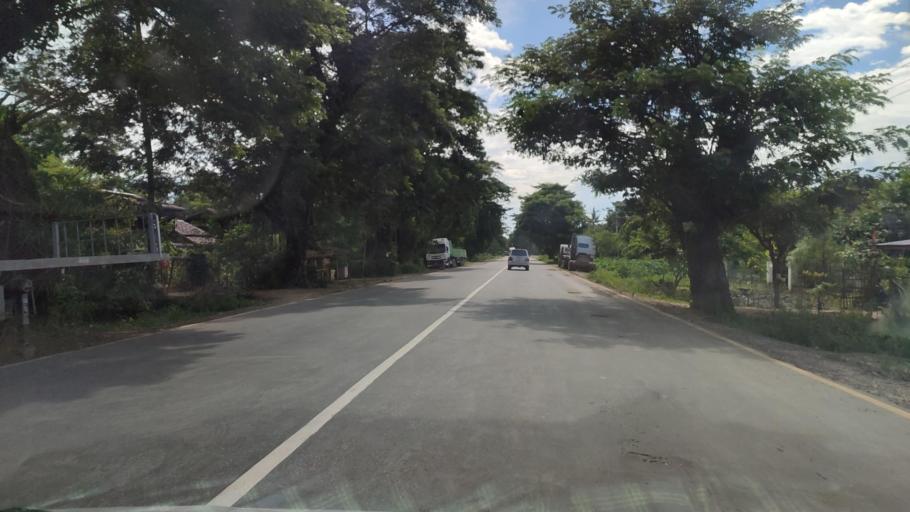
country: MM
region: Bago
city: Nyaunglebin
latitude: 18.1847
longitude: 96.5822
